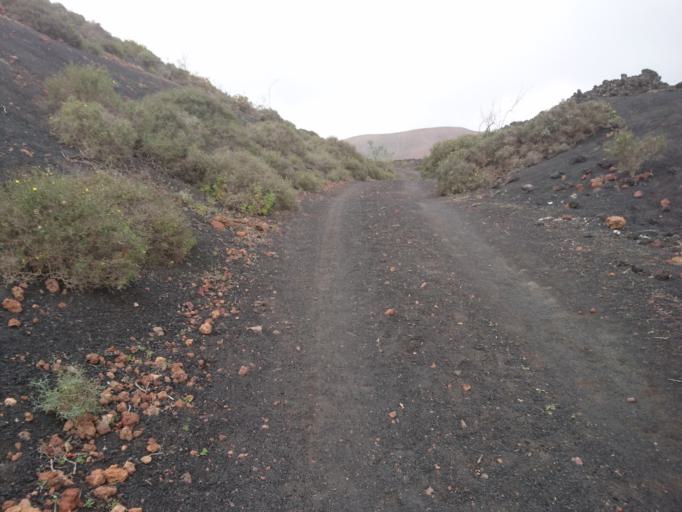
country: ES
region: Canary Islands
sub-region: Provincia de Las Palmas
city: Tinajo
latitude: 29.0148
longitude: -13.6923
